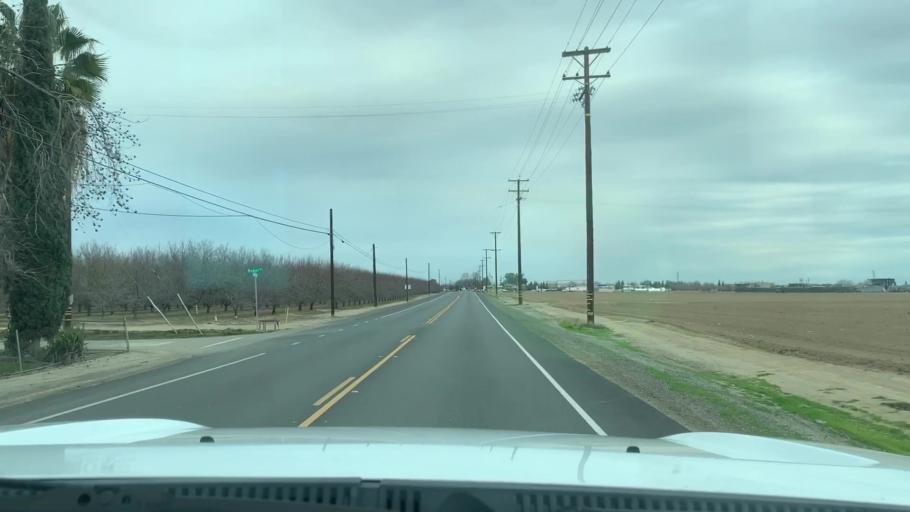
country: US
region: California
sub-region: Kern County
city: Shafter
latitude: 35.4343
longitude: -119.2518
